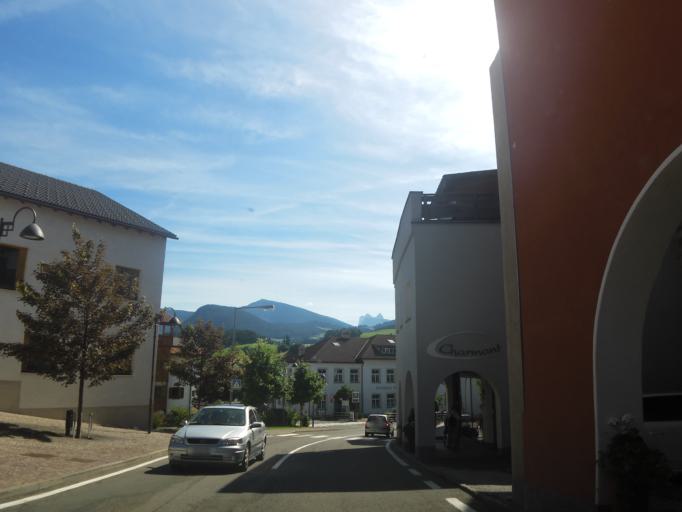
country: IT
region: Trentino-Alto Adige
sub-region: Bolzano
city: Castelrotto
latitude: 46.5670
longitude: 11.5607
